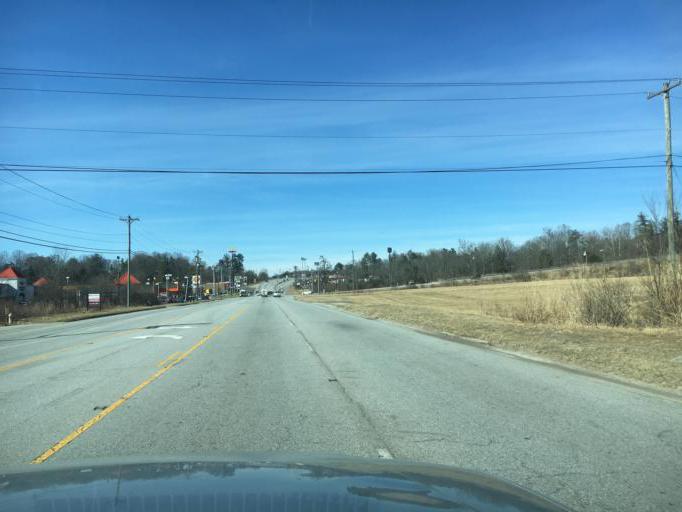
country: US
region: North Carolina
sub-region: Henderson County
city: Mountain Home
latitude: 35.3937
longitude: -82.5035
